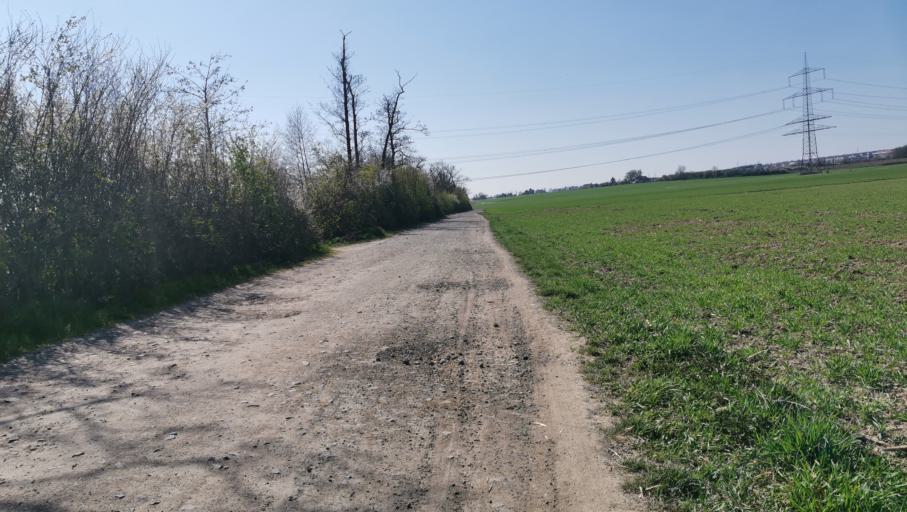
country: DE
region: Hesse
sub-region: Regierungsbezirk Darmstadt
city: Karben
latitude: 50.2199
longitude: 8.7622
